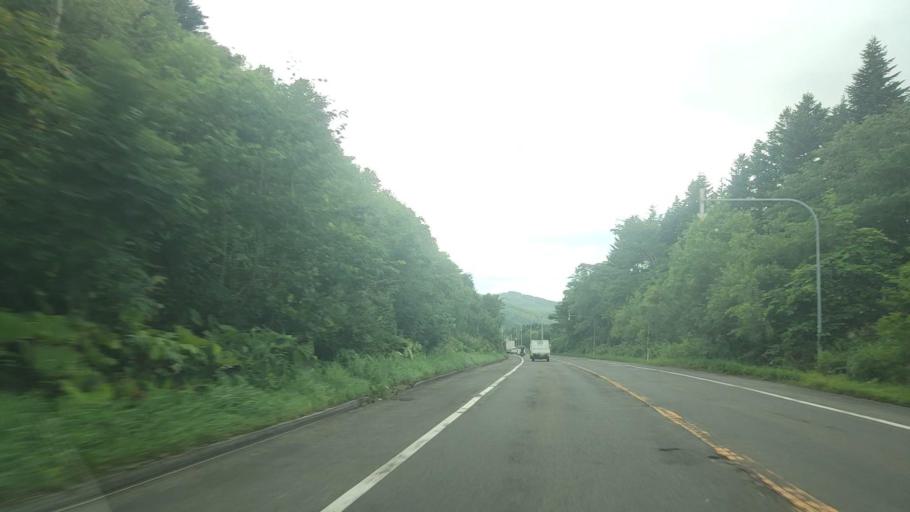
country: JP
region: Hokkaido
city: Niseko Town
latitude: 42.5934
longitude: 140.5270
